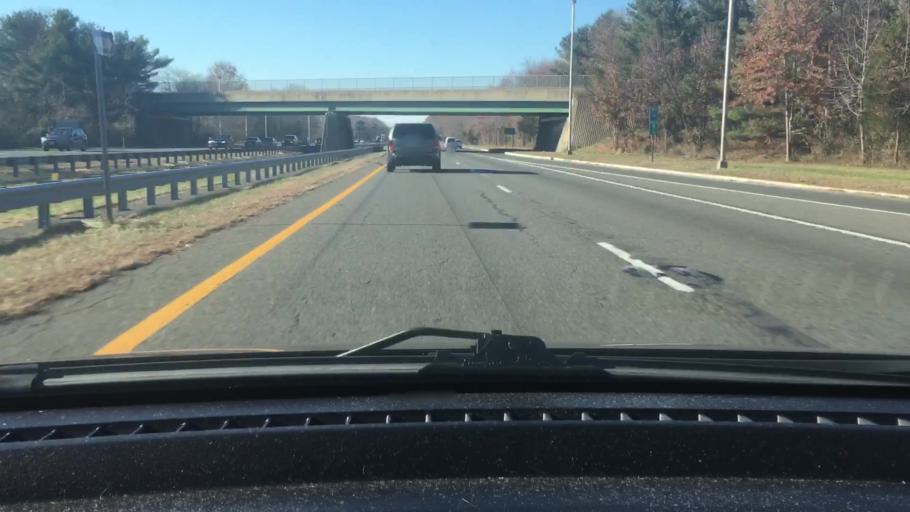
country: US
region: New Jersey
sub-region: Monmouth County
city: Allentown
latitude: 40.1856
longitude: -74.5691
